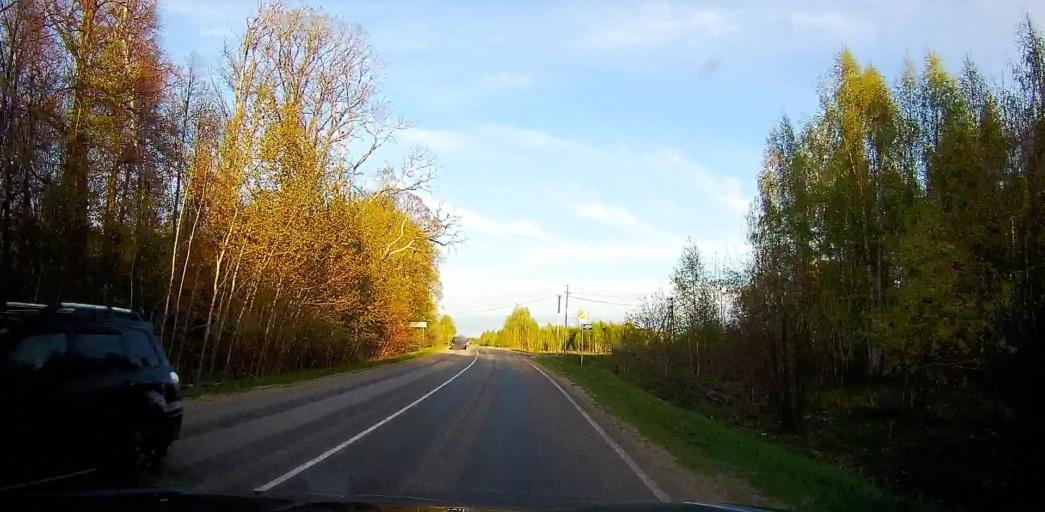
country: RU
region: Moskovskaya
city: Meshcherino
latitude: 55.2511
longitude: 38.2833
